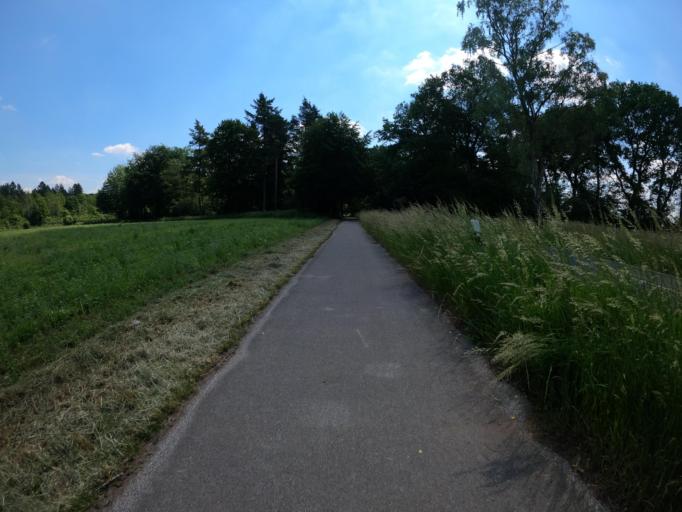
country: DE
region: North Rhine-Westphalia
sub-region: Regierungsbezirk Dusseldorf
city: Hunxe
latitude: 51.7123
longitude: 6.7751
